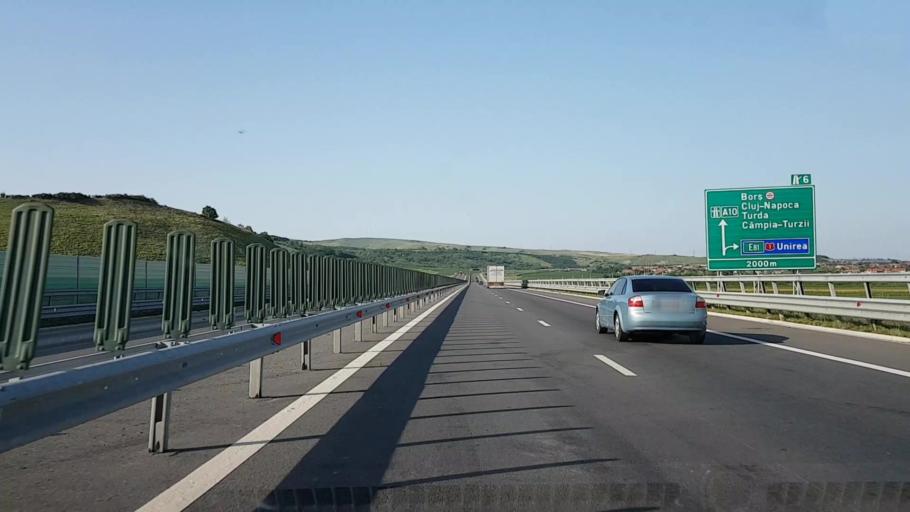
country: RO
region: Alba
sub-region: Comuna Miraslau
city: Miraslau
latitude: 46.3729
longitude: 23.7464
